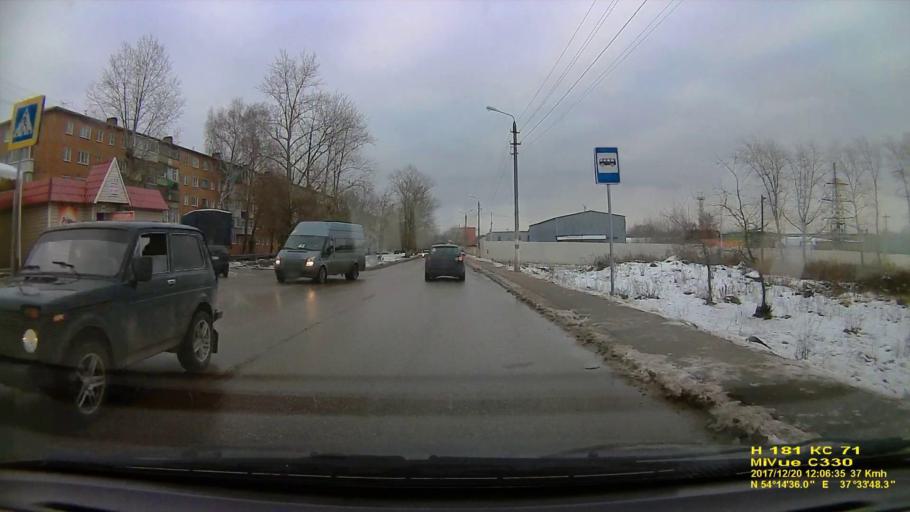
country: RU
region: Tula
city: Gorelki
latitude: 54.2433
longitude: 37.5635
